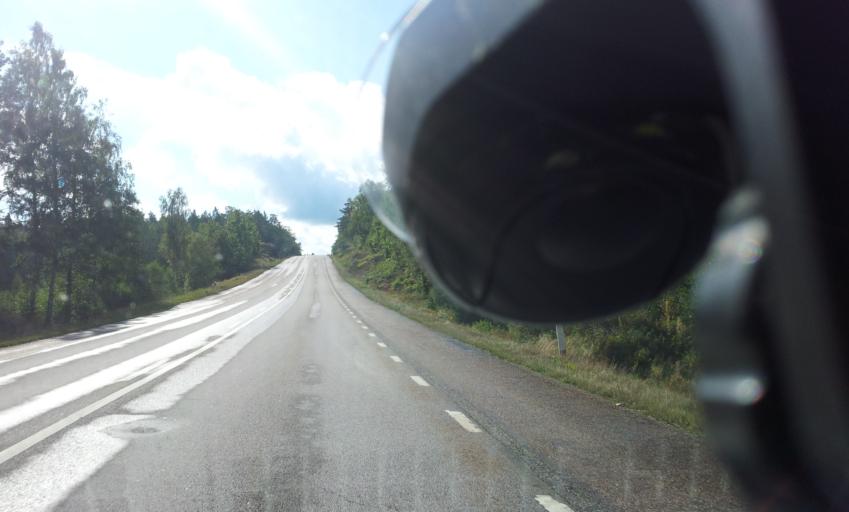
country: SE
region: Kalmar
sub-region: Oskarshamns Kommun
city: Oskarshamn
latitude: 57.4675
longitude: 16.5170
